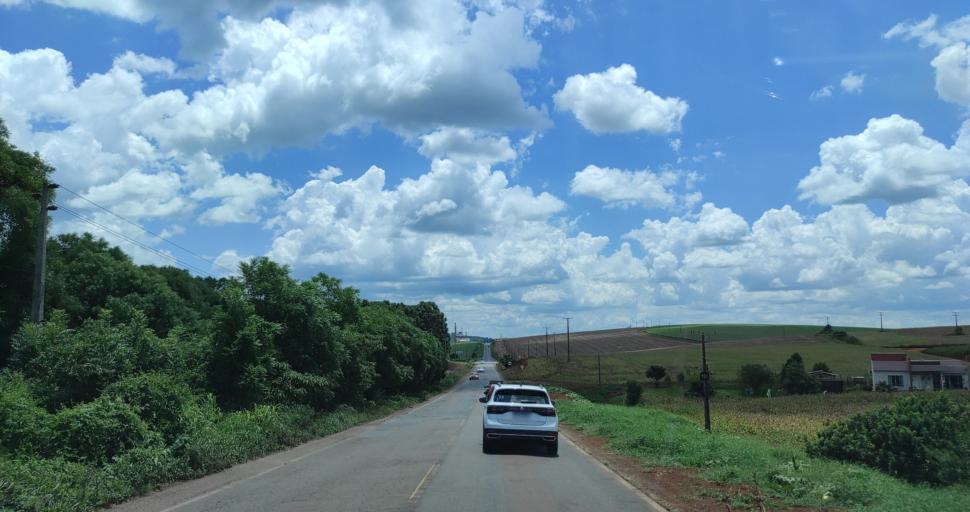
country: BR
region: Santa Catarina
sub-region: Xanxere
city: Xanxere
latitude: -26.7727
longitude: -52.4063
